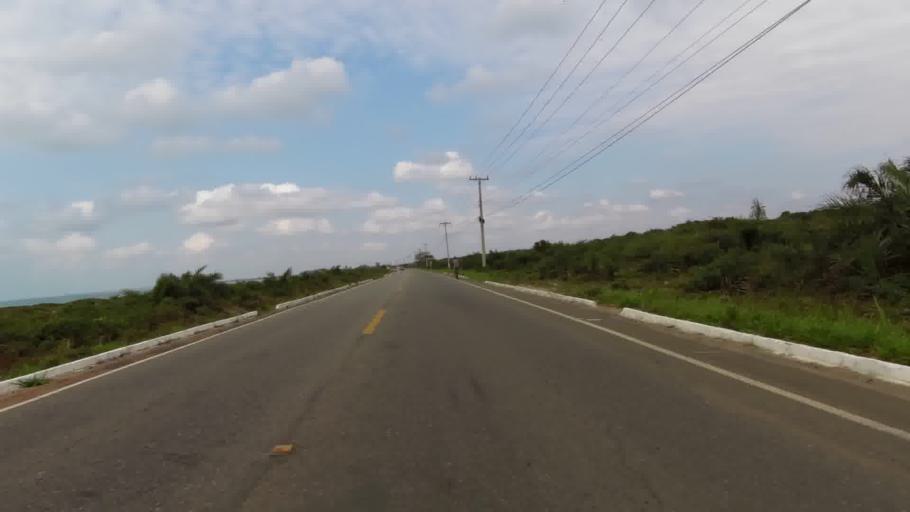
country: BR
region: Espirito Santo
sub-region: Itapemirim
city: Itapemirim
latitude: -20.9187
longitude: -40.7904
